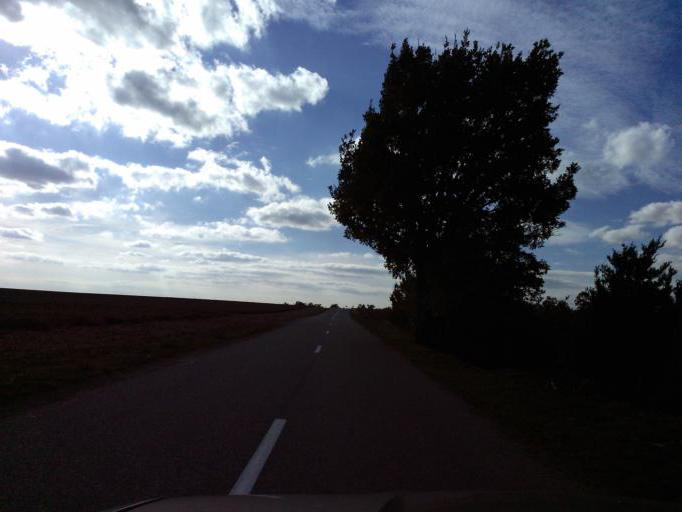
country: FR
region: Provence-Alpes-Cote d'Azur
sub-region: Departement des Alpes-de-Haute-Provence
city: Riez
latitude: 43.8952
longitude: 6.0763
